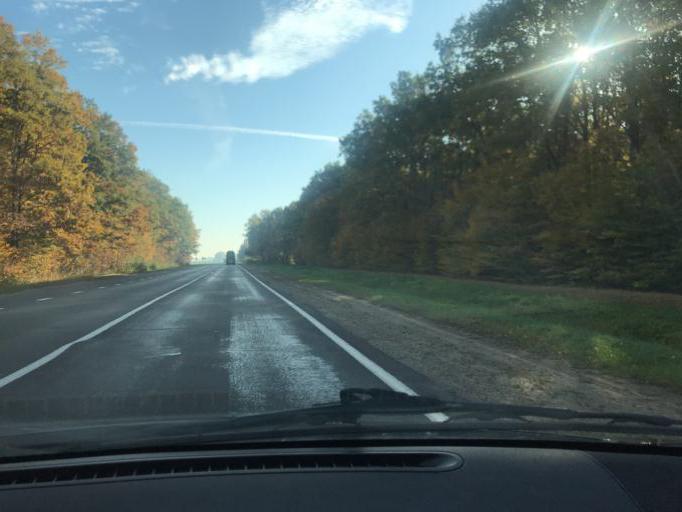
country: BY
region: Brest
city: Ivanava
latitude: 52.1522
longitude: 25.3678
